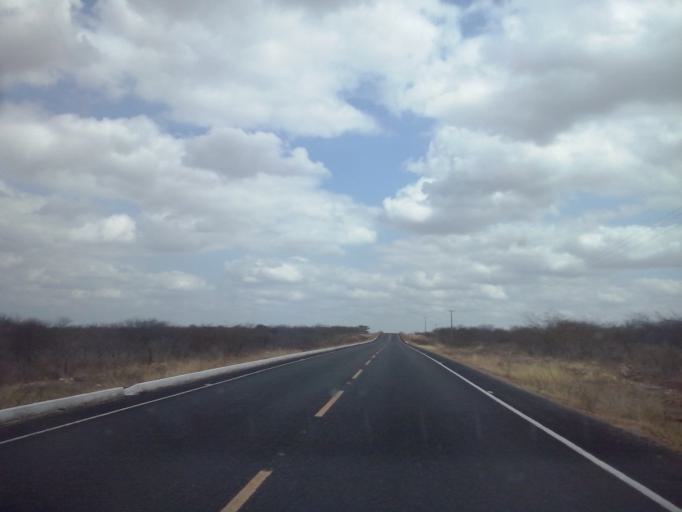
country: BR
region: Paraiba
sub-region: Pombal
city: Pombal
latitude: -6.8426
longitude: -37.5658
